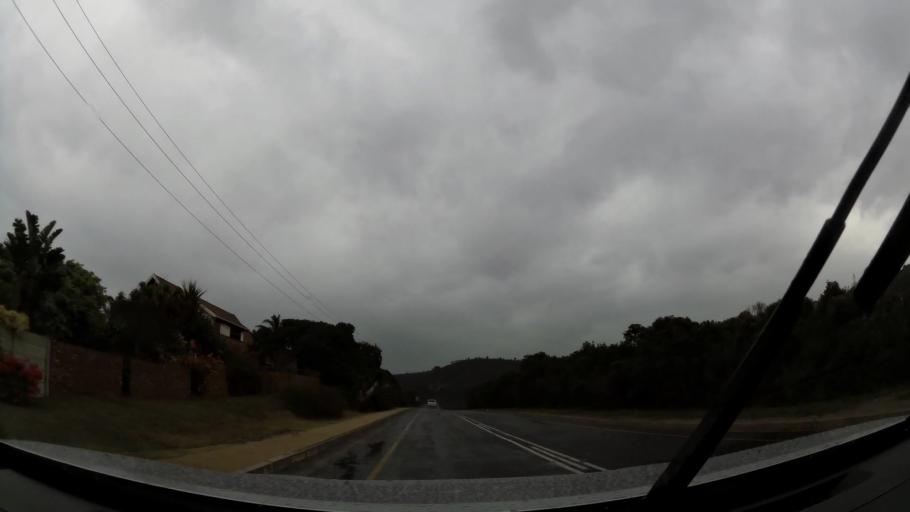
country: ZA
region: Western Cape
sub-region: Eden District Municipality
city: Mossel Bay
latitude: -34.0506
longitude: 22.2448
